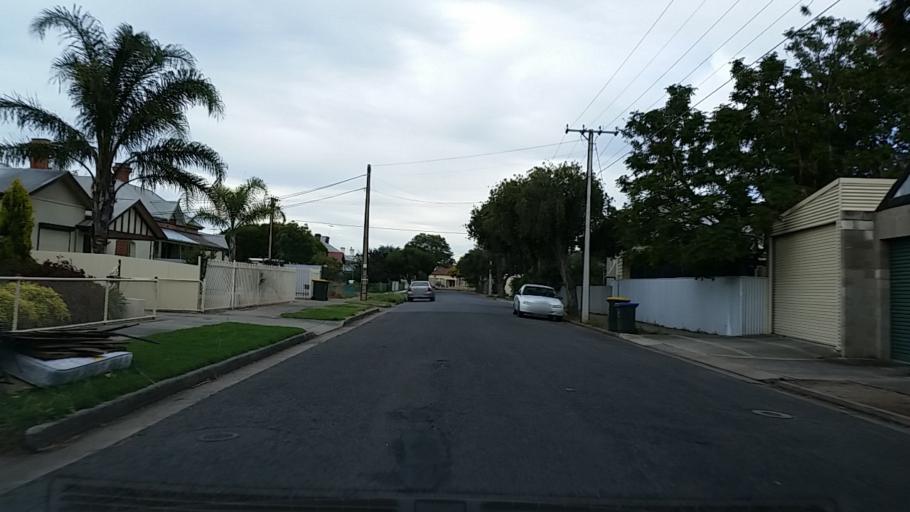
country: AU
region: South Australia
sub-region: Charles Sturt
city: Allenby Gardens
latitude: -34.9009
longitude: 138.5605
